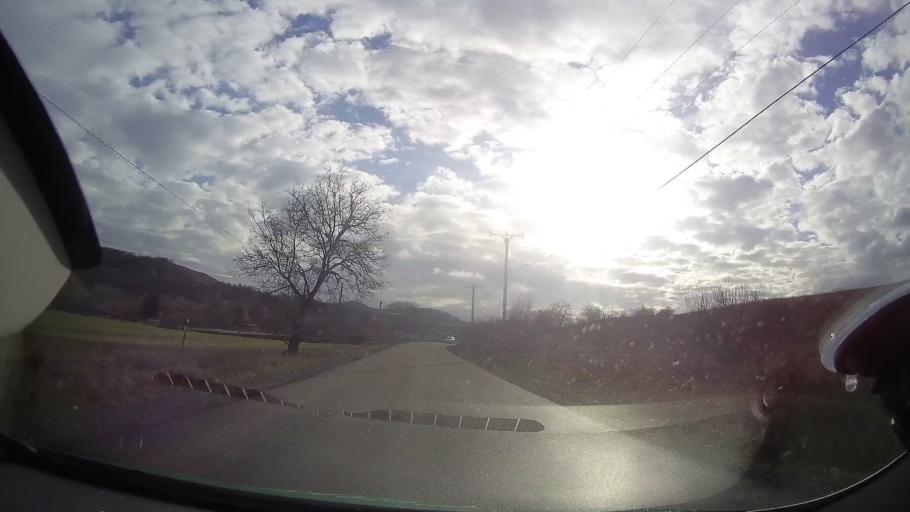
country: RO
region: Cluj
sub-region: Comuna Floresti
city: Luna de Sus
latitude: 46.7186
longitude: 23.4246
